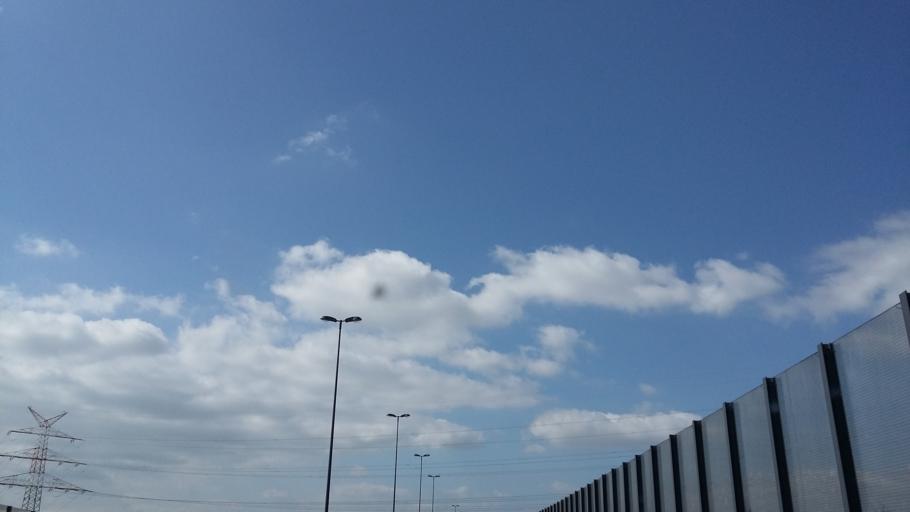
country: DE
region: Bremen
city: Bremen
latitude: 53.0628
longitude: 8.7822
